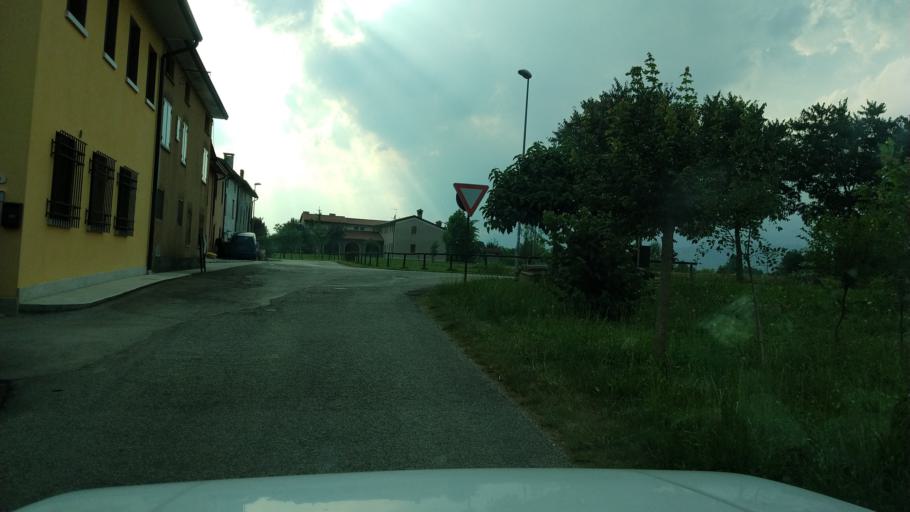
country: IT
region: Veneto
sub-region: Provincia di Vicenza
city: Schiavon
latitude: 45.7075
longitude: 11.6556
